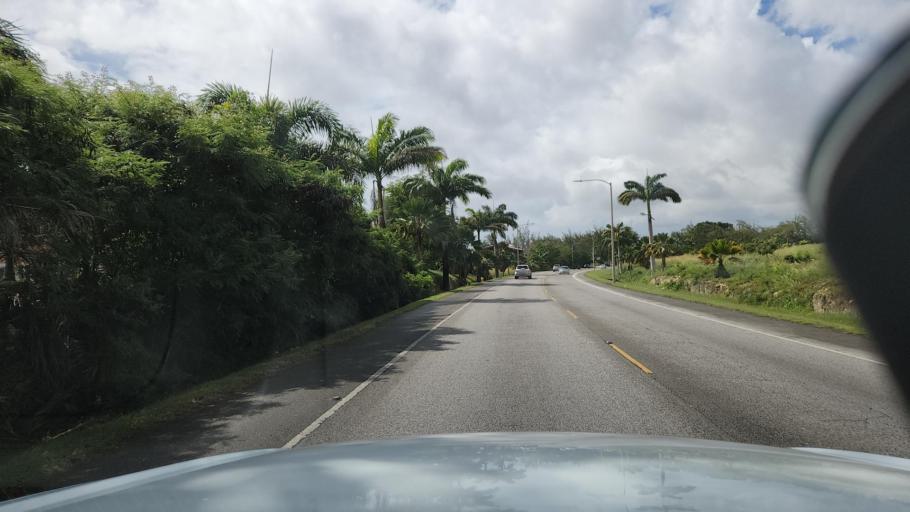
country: BB
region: Christ Church
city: Oistins
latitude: 13.0783
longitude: -59.5236
